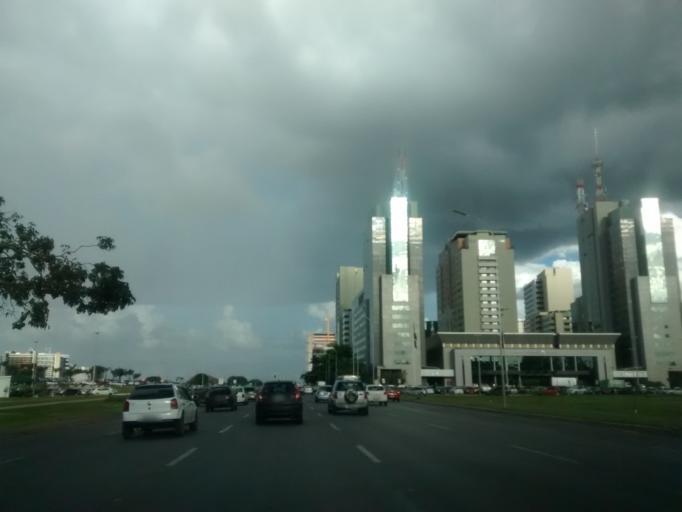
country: BR
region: Federal District
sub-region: Brasilia
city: Brasilia
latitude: -15.7915
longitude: -47.8961
